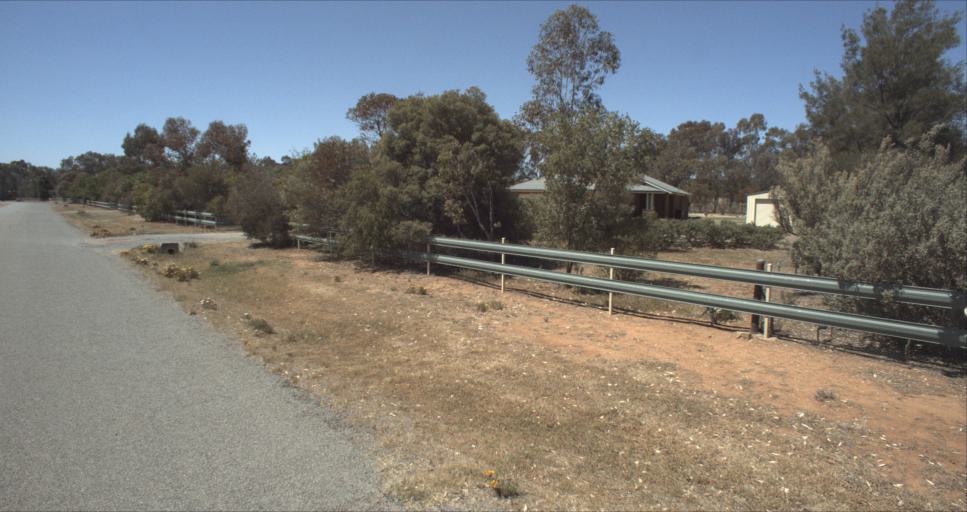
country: AU
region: New South Wales
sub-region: Leeton
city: Leeton
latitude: -34.5305
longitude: 146.3963
